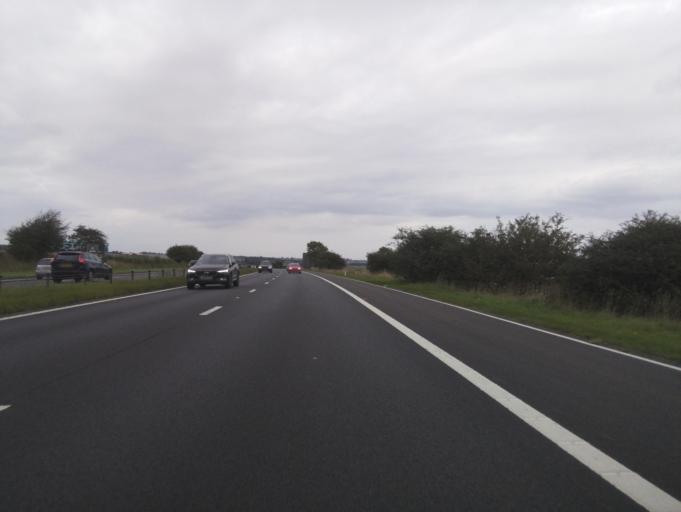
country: GB
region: England
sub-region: County Durham
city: Bishop Middleham
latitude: 54.6607
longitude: -1.5004
